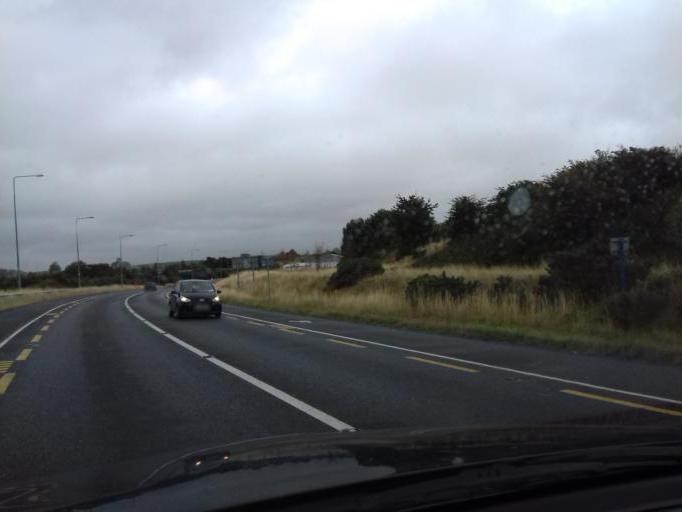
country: IE
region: Leinster
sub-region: County Carlow
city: Bagenalstown
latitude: 52.7644
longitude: -6.9564
